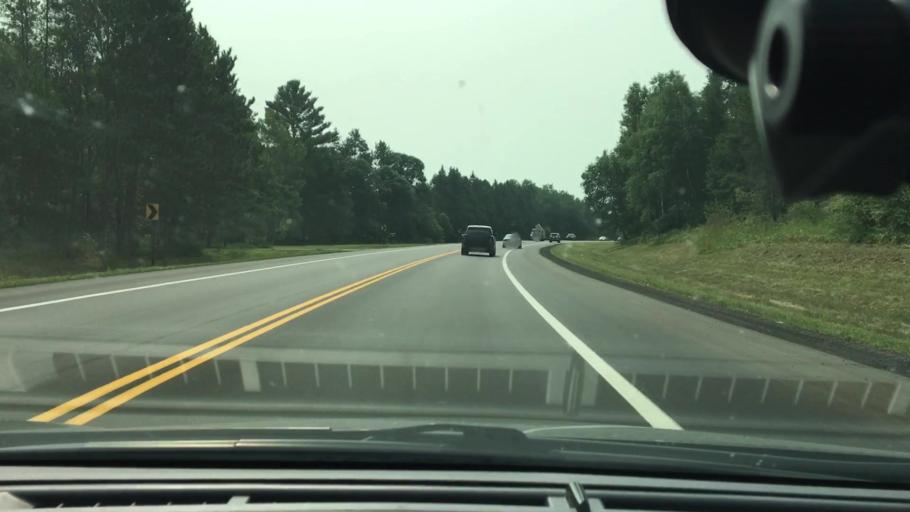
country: US
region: Minnesota
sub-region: Crow Wing County
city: Brainerd
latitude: 46.4134
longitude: -94.1767
